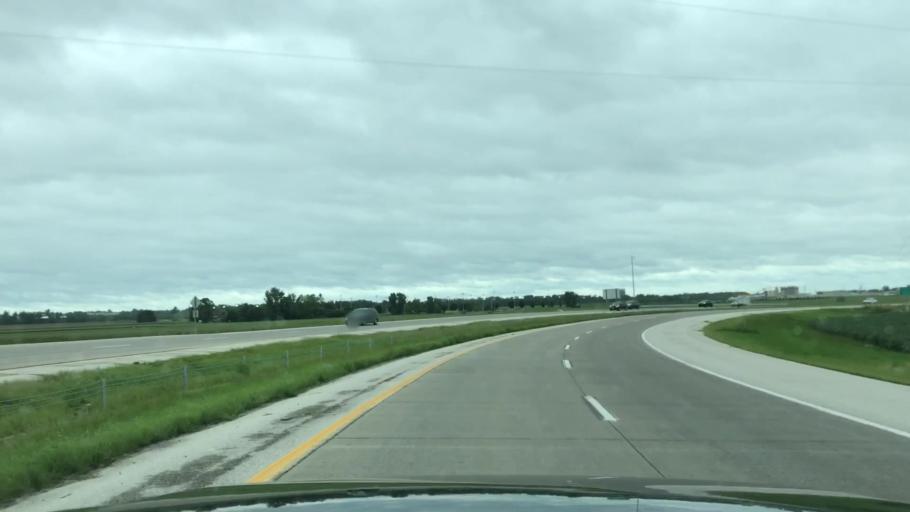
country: US
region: Missouri
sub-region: Saint Charles County
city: Saint Charles
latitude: 38.7255
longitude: -90.4985
